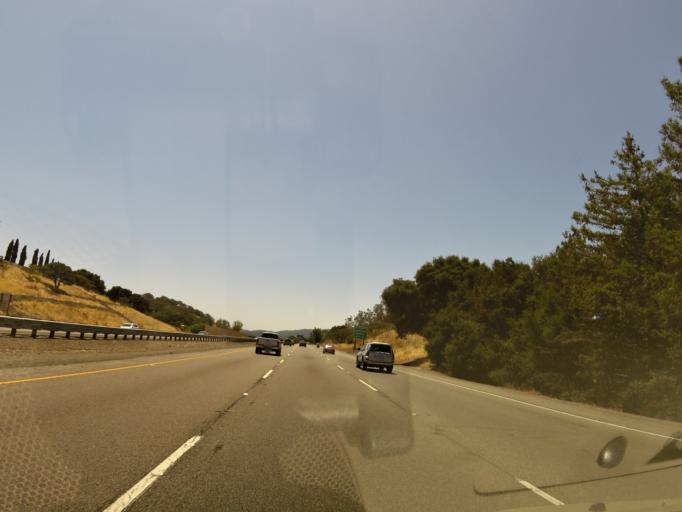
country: US
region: California
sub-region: Marin County
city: Novato
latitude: 38.1132
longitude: -122.5645
